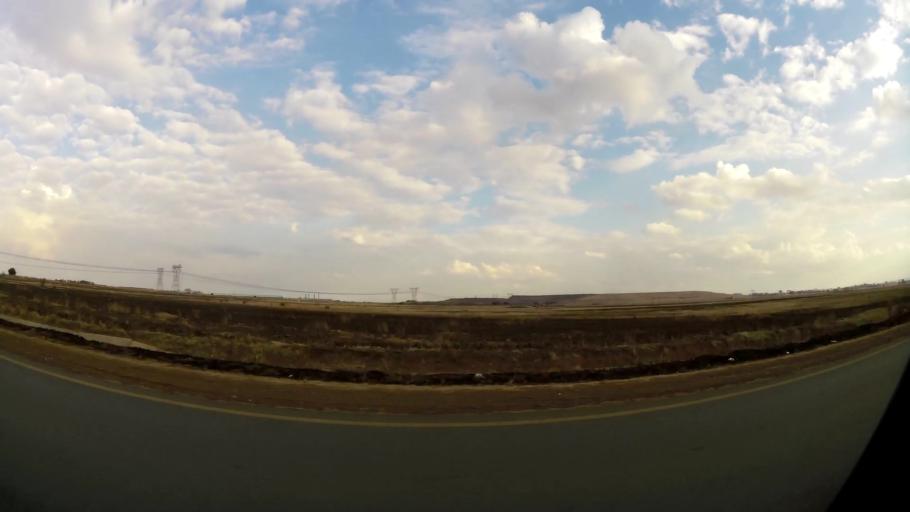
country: ZA
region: Gauteng
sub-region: Sedibeng District Municipality
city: Vanderbijlpark
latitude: -26.6193
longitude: 27.8246
